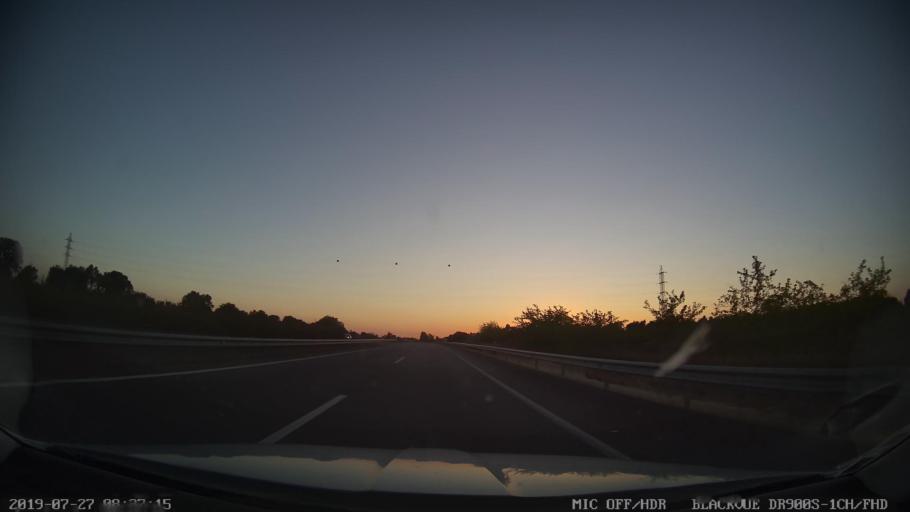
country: ES
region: Extremadura
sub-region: Provincia de Badajoz
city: Talavera La Real
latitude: 38.8719
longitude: -6.8588
